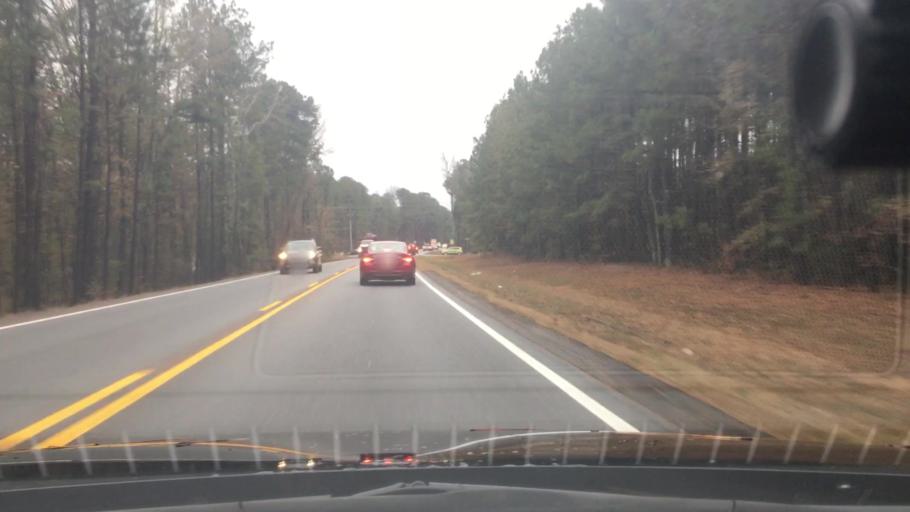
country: US
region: Georgia
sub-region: Fayette County
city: Peachtree City
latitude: 33.3532
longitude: -84.6584
